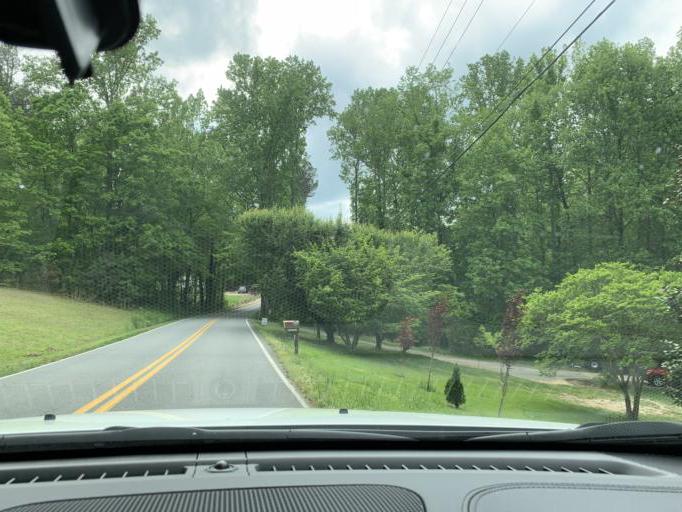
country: US
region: Georgia
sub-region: Gwinnett County
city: Suwanee
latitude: 34.1010
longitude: -84.1315
